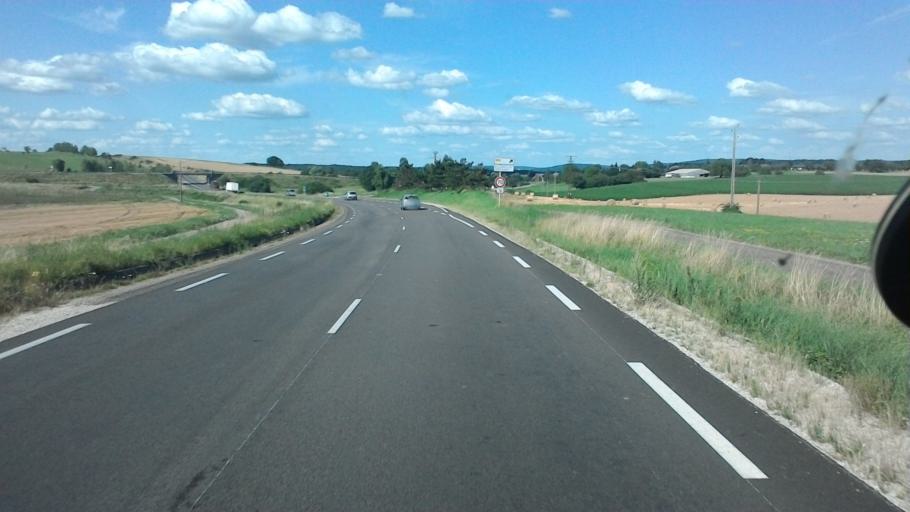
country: FR
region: Franche-Comte
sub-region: Departement de la Haute-Saone
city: Gy
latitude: 47.4779
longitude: 5.9326
